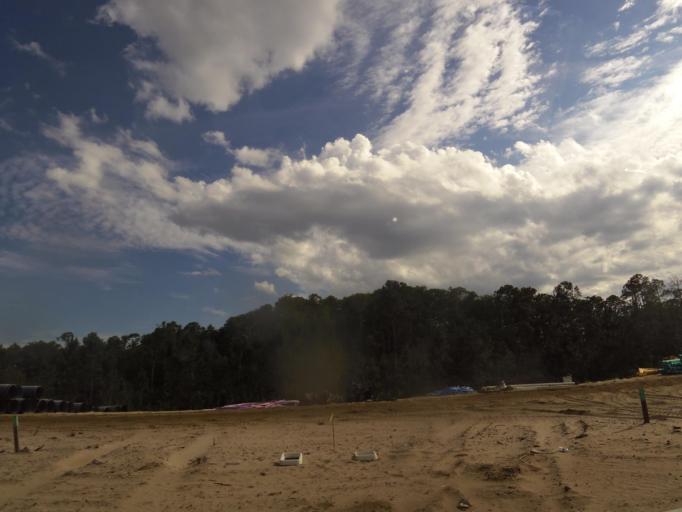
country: US
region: Florida
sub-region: Saint Johns County
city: Palm Valley
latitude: 30.1794
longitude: -81.5068
